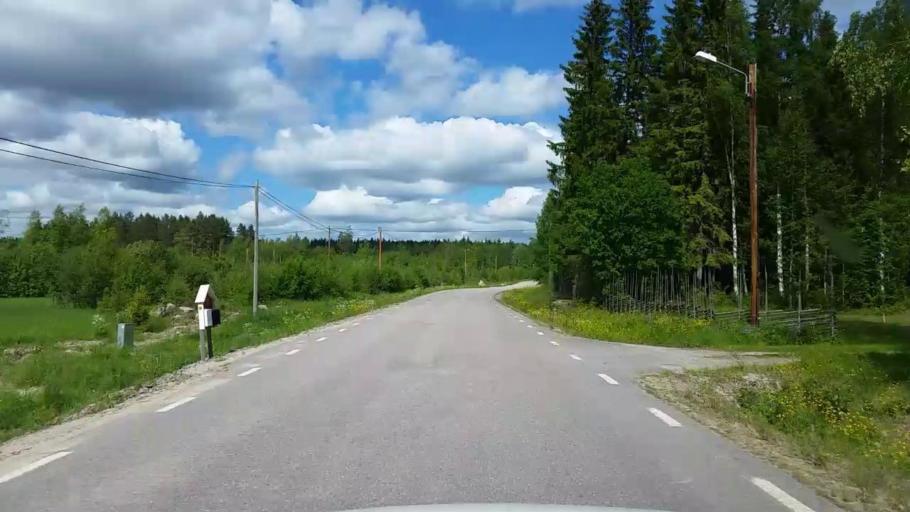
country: SE
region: Gaevleborg
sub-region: Ovanakers Kommun
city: Alfta
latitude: 61.4028
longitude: 16.0504
